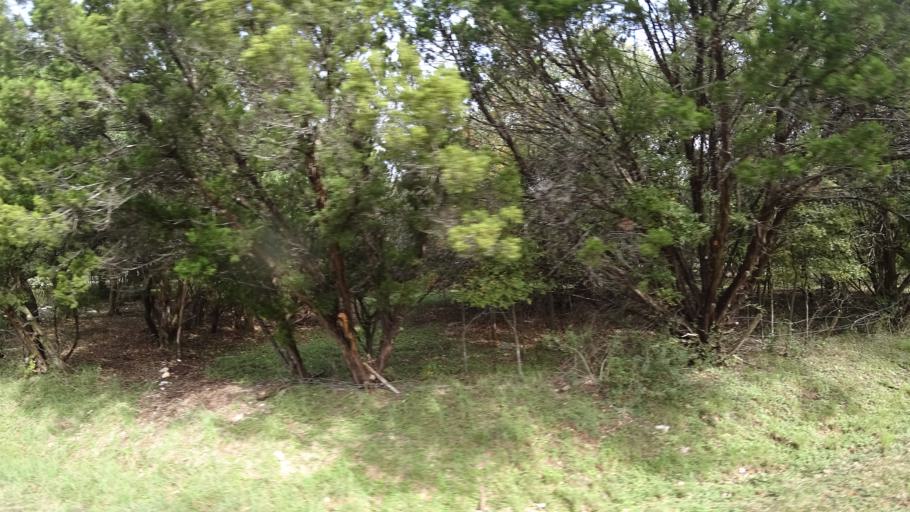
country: US
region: Texas
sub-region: Travis County
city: Wells Branch
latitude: 30.4301
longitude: -97.7059
